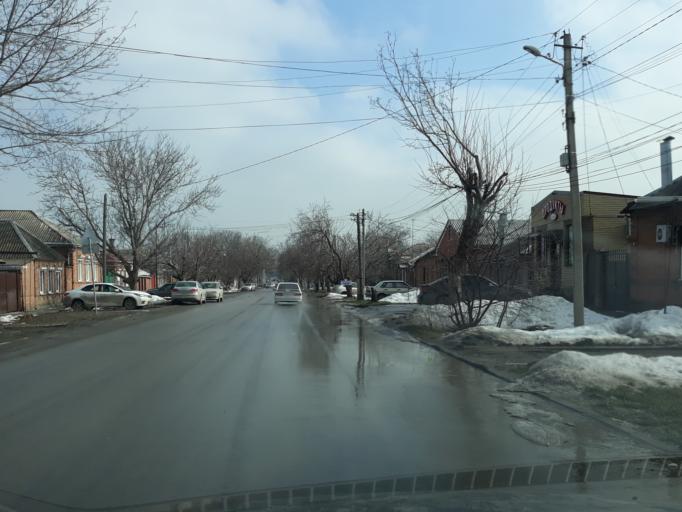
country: RU
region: Rostov
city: Taganrog
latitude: 47.2128
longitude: 38.9073
